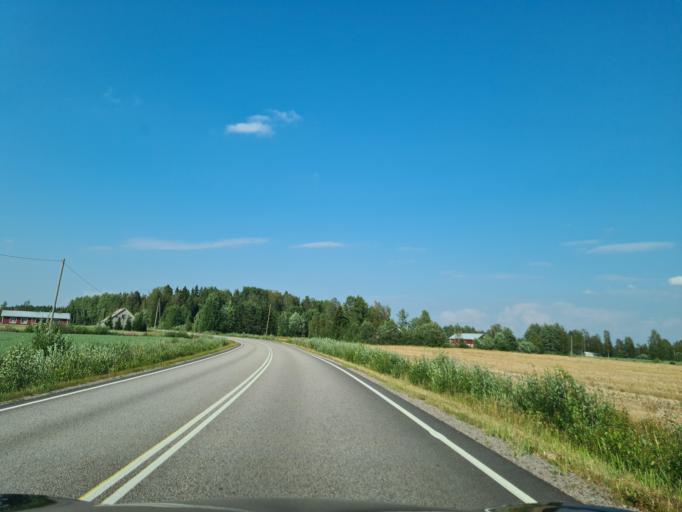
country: FI
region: Satakunta
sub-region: Pohjois-Satakunta
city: Karvia
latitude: 62.2091
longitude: 22.6043
